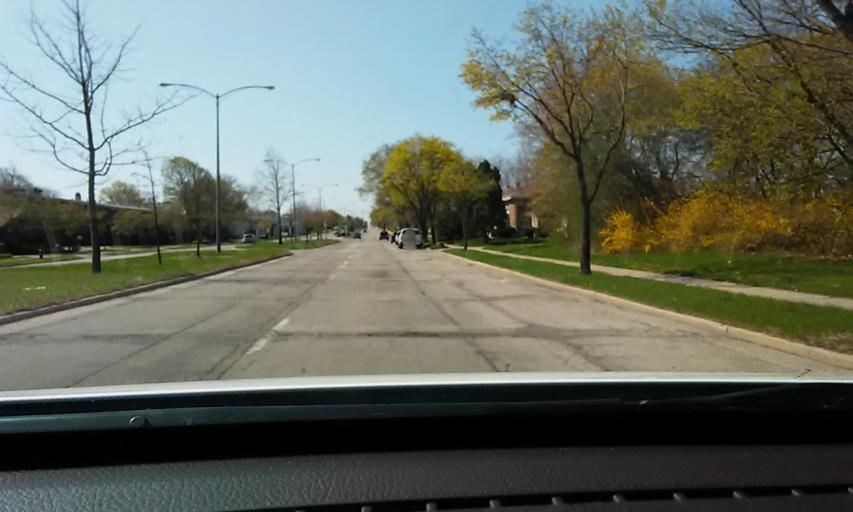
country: US
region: Wisconsin
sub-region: Milwaukee County
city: West Milwaukee
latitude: 42.9972
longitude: -87.9877
